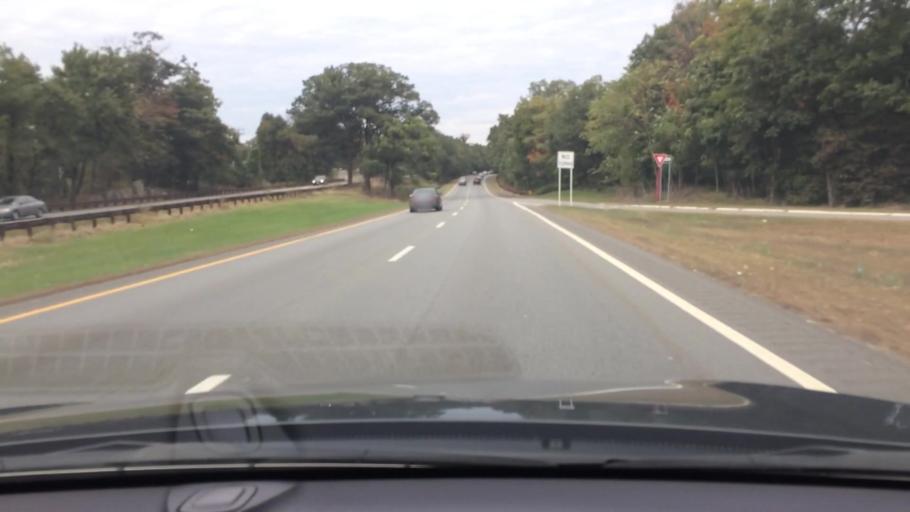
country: US
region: New Jersey
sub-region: Bergen County
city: Englewood Cliffs
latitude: 40.8930
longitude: -73.9414
